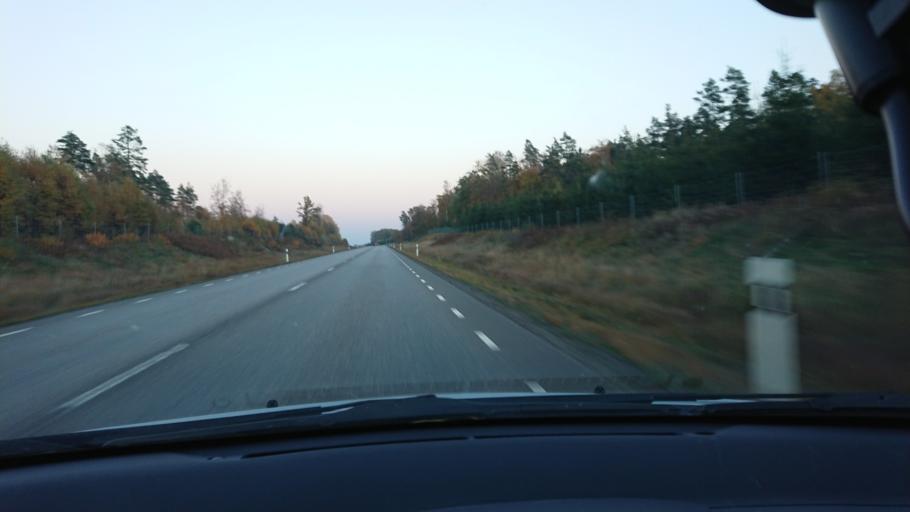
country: SE
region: Kronoberg
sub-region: Markaryds Kommun
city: Stromsnasbruk
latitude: 56.7518
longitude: 13.5213
